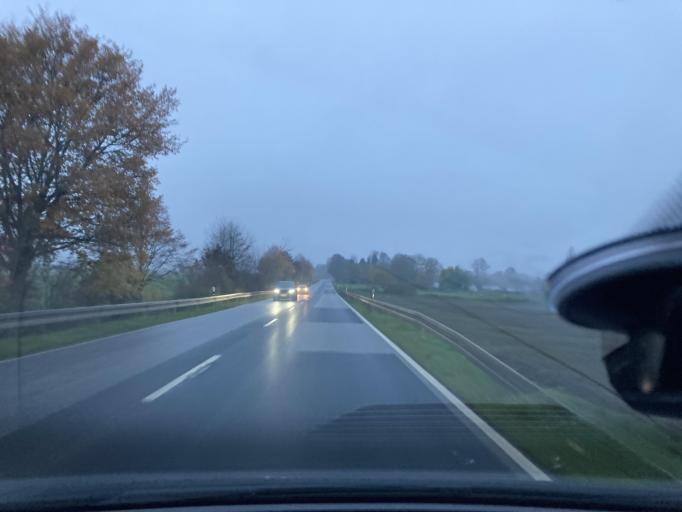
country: DE
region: Hesse
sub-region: Regierungsbezirk Darmstadt
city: Karben
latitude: 50.2288
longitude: 8.7228
